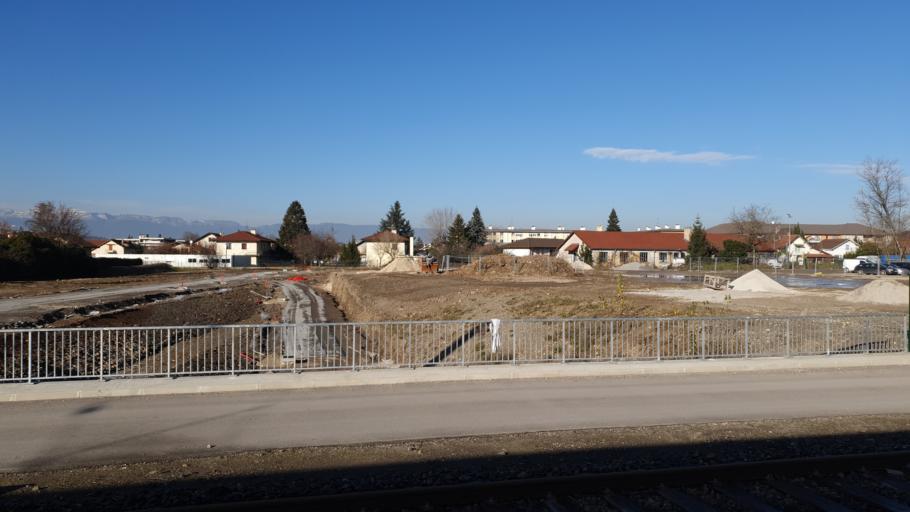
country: FR
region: Rhone-Alpes
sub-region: Departement de la Haute-Savoie
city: Annemasse
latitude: 46.2000
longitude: 6.2362
